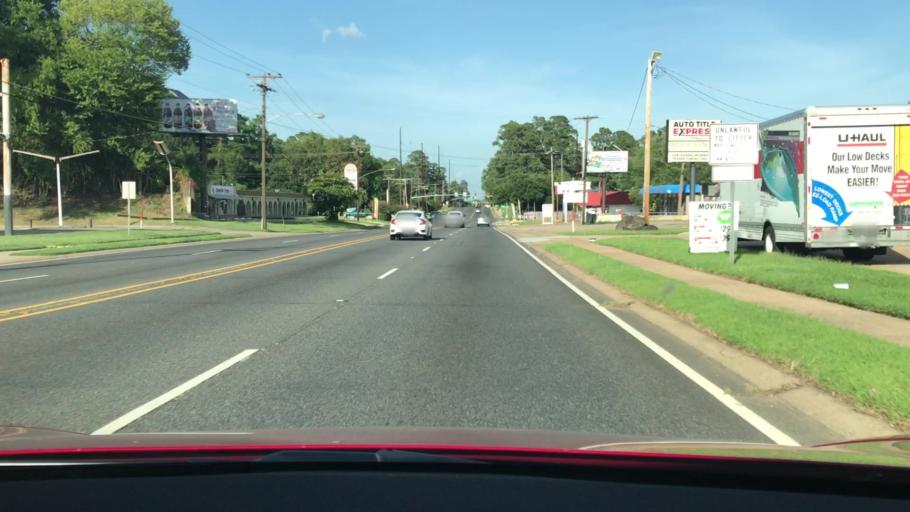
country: US
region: Louisiana
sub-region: Bossier Parish
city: Bossier City
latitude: 32.4424
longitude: -93.7411
